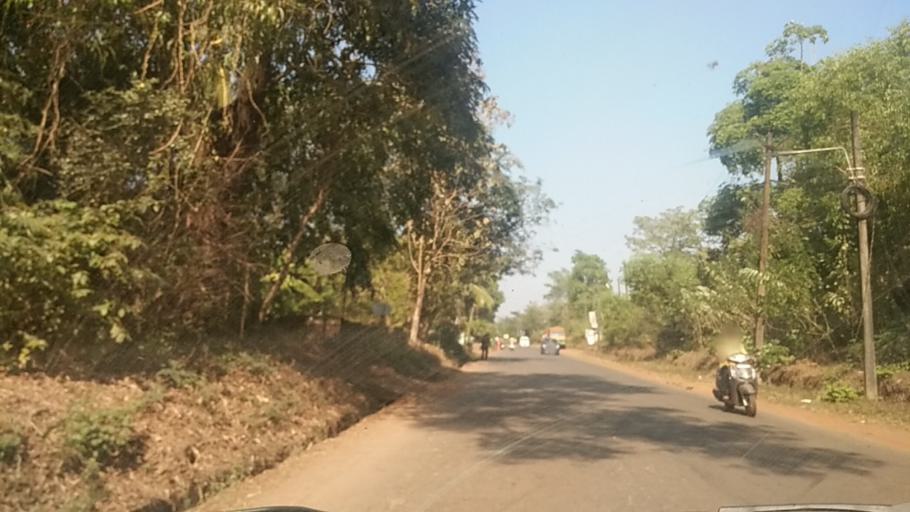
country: IN
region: Goa
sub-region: South Goa
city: Sanvordem
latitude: 15.2402
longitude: 74.1224
